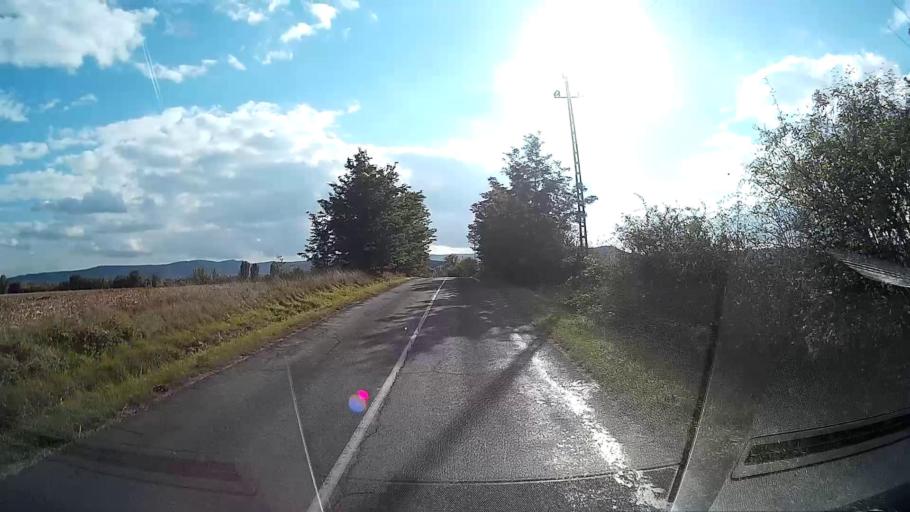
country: HU
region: Pest
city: Pilisvorosvar
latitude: 47.6369
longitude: 18.9044
